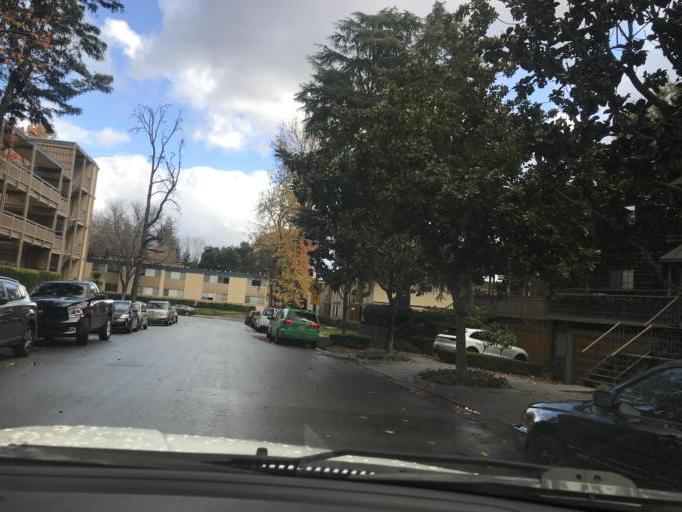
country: US
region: California
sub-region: Santa Clara County
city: Buena Vista
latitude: 37.2956
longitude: -121.9098
